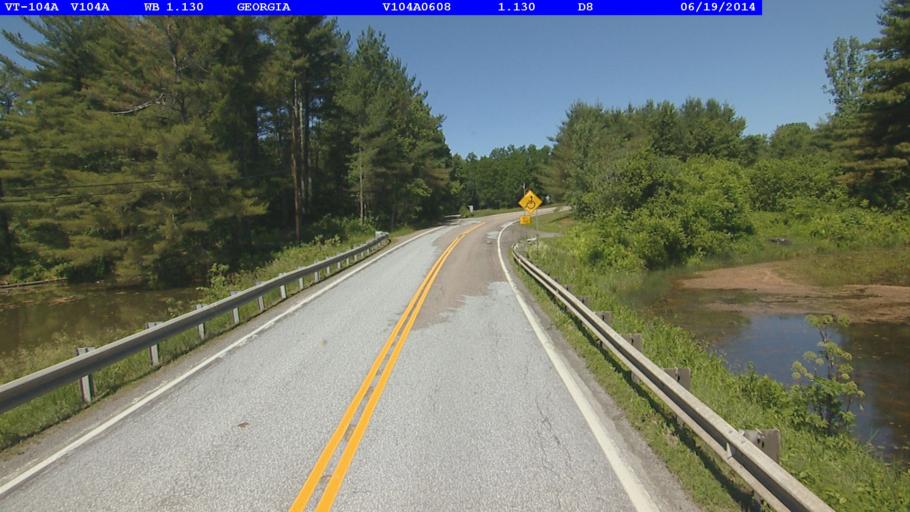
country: US
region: Vermont
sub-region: Chittenden County
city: Milton
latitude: 44.6833
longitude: -73.0929
